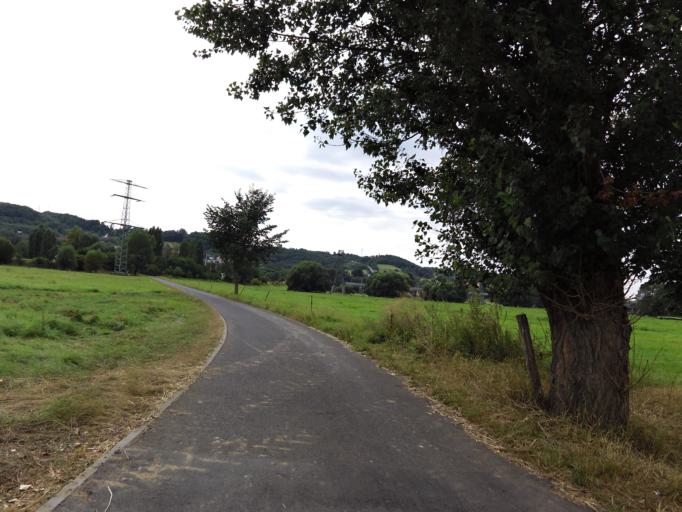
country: DE
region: Saxony
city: Coswig
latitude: 51.0968
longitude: 13.6139
